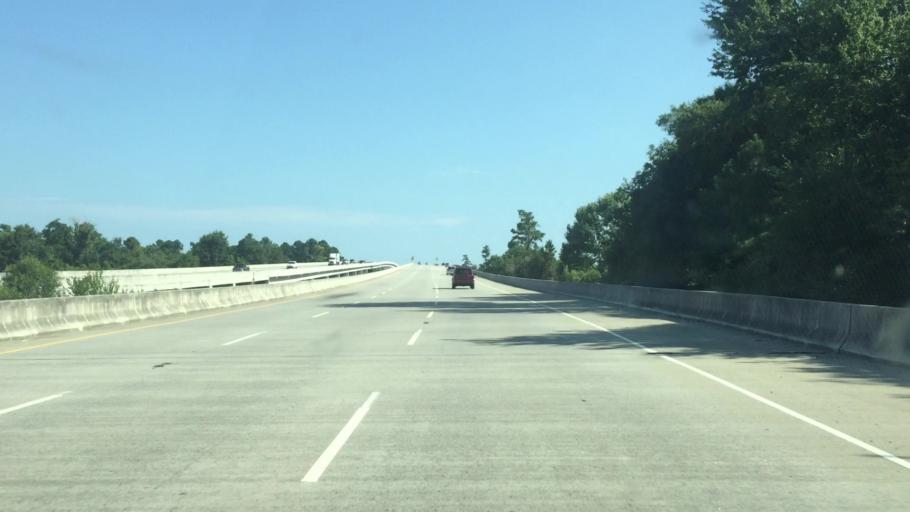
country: US
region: South Carolina
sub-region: Horry County
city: North Myrtle Beach
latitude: 33.7950
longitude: -78.7790
